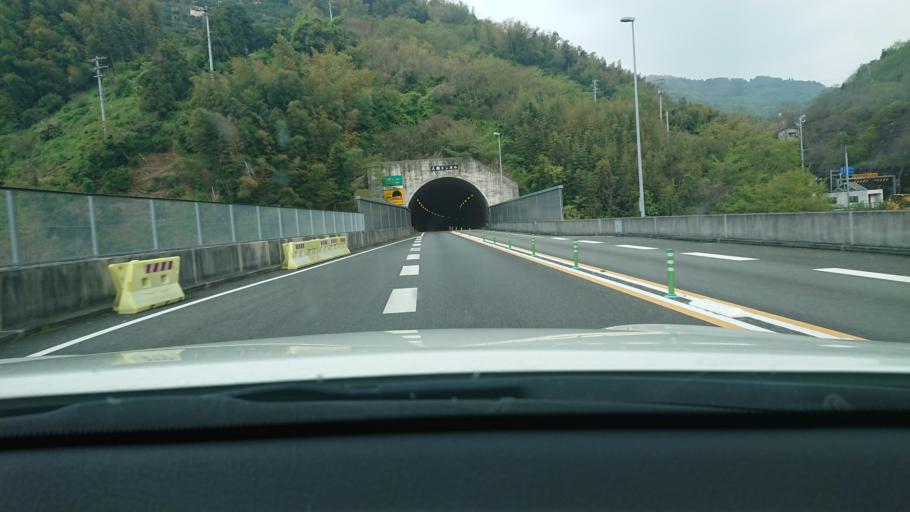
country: JP
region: Ehime
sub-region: Nishiuwa-gun
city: Ikata-cho
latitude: 33.4695
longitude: 132.4242
